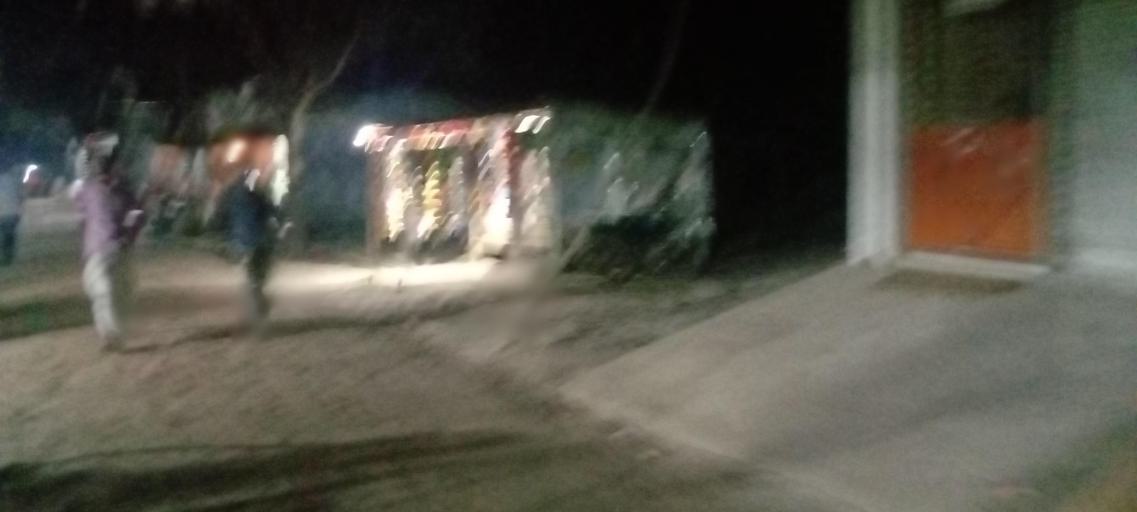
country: BD
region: Dhaka
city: Sakhipur
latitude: 24.4513
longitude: 90.2791
